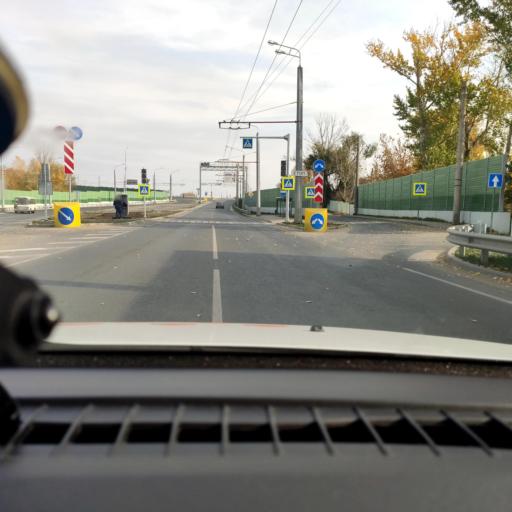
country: RU
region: Samara
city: Rozhdestveno
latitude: 53.1650
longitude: 50.0788
